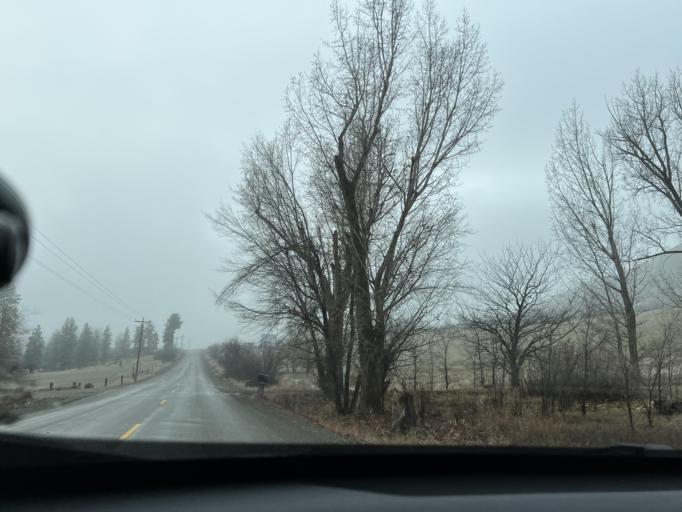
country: US
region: Washington
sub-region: Okanogan County
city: Brewster
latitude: 48.4498
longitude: -120.2027
